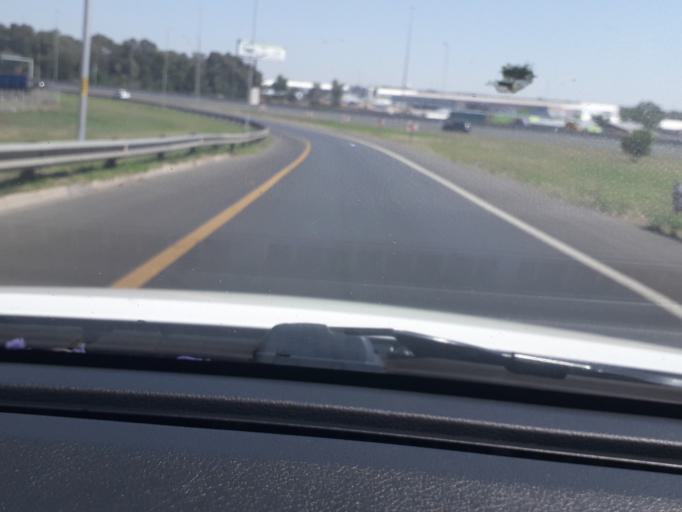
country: ZA
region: Gauteng
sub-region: Ekurhuleni Metropolitan Municipality
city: Boksburg
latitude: -26.1735
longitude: 28.2402
